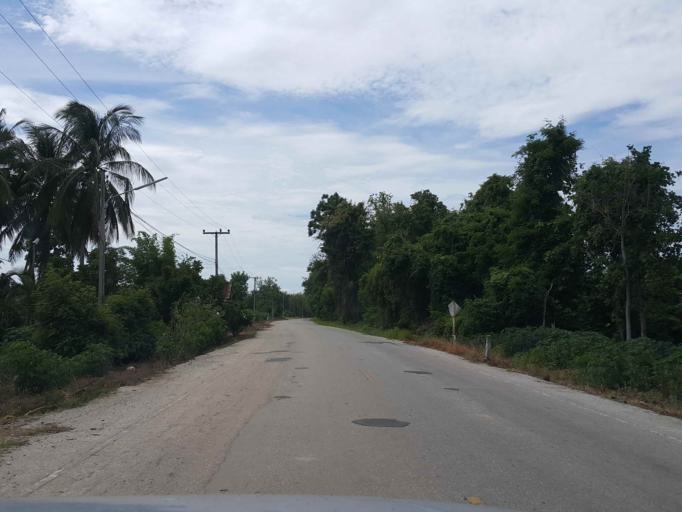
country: TH
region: Sukhothai
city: Ban Dan Lan Hoi
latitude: 17.0856
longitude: 99.4777
